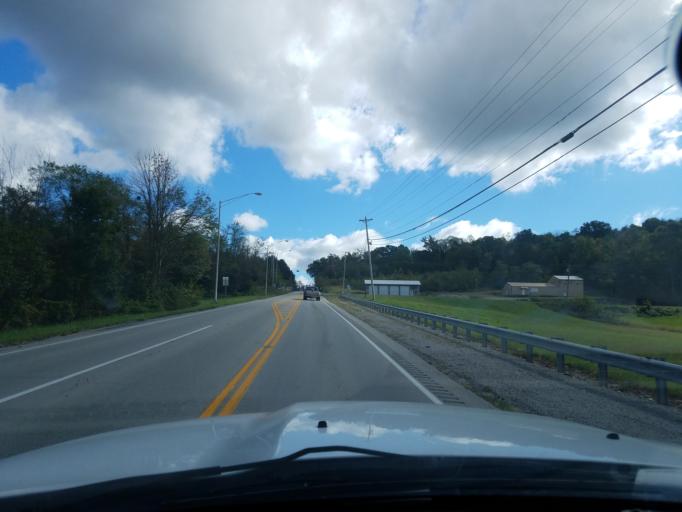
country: US
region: Kentucky
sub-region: Rockcastle County
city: Mount Vernon
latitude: 37.3506
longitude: -84.3608
